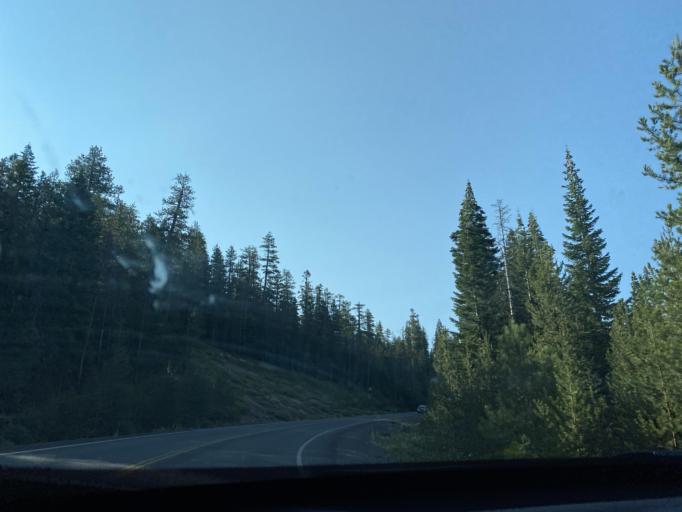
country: US
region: Oregon
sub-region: Deschutes County
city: Three Rivers
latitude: 43.7071
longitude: -121.3173
